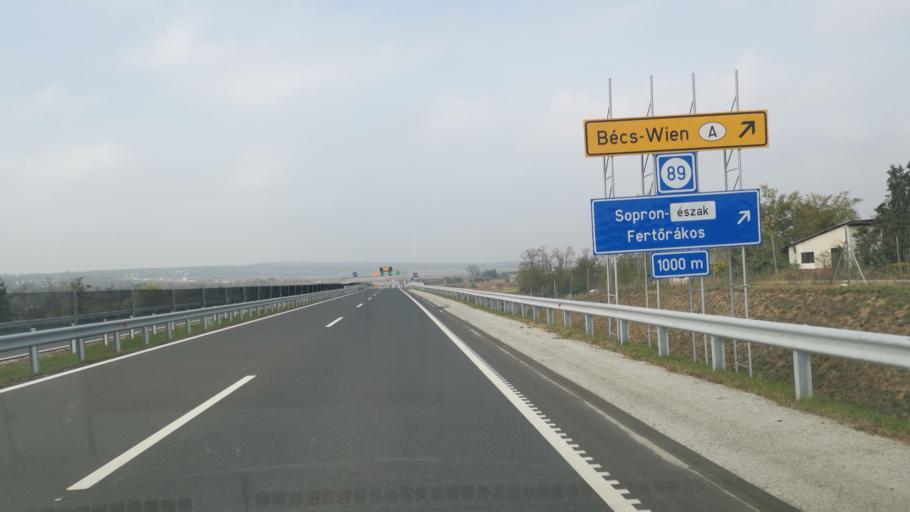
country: HU
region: Gyor-Moson-Sopron
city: Sopron
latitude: 47.6985
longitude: 16.6167
